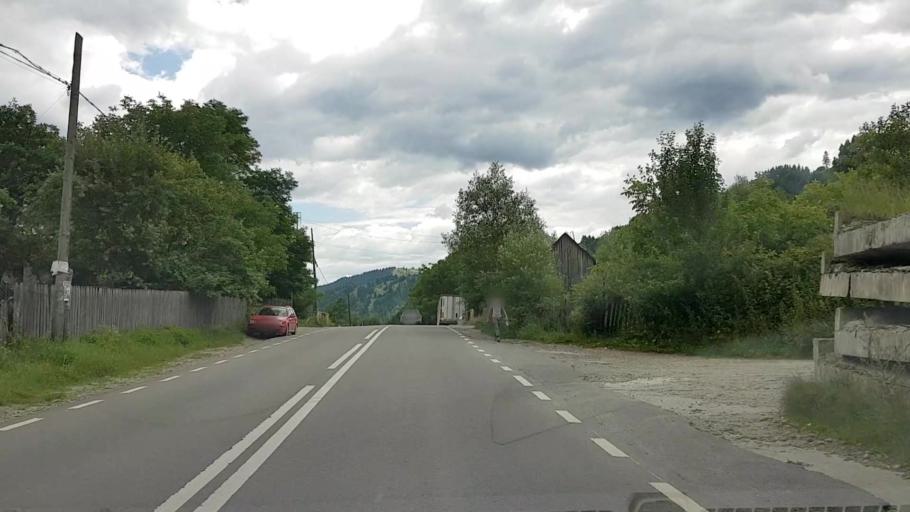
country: RO
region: Neamt
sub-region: Comuna Farcasa
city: Farcasa
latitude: 47.1677
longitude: 25.8042
